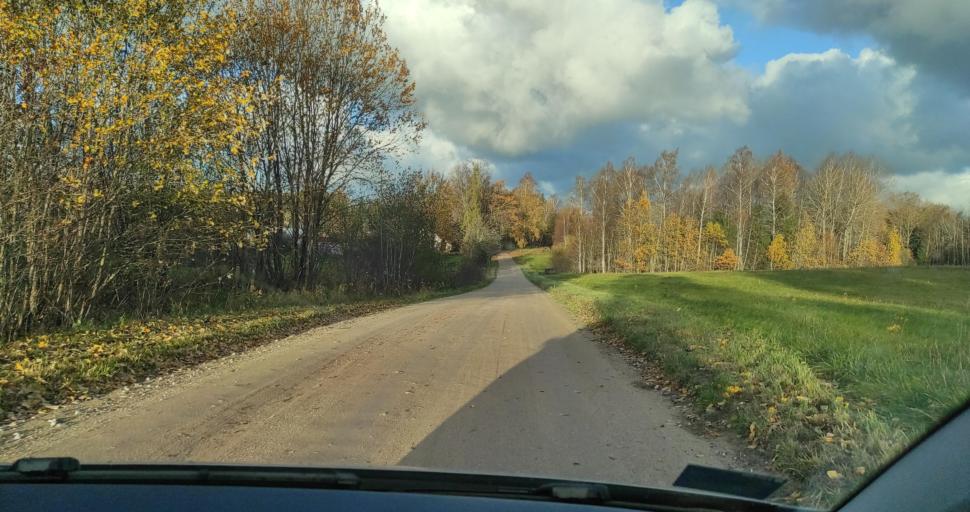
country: LV
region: Alsunga
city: Alsunga
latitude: 56.9491
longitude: 21.6332
